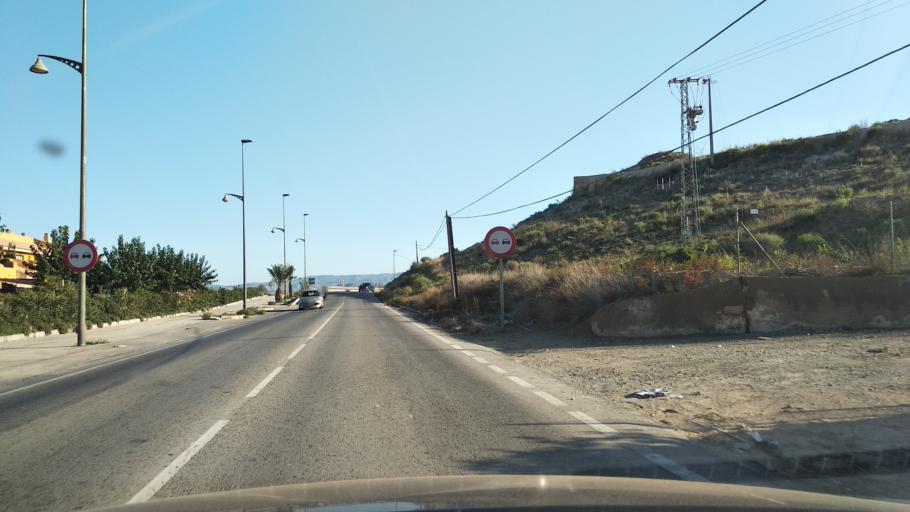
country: ES
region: Murcia
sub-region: Murcia
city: Santomera
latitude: 38.0573
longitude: -1.0529
